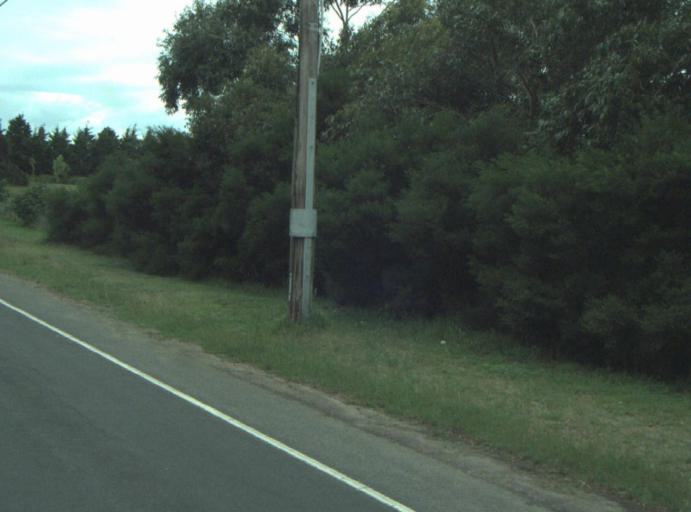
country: AU
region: Victoria
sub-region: Greater Geelong
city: Leopold
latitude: -38.1969
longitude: 144.4674
